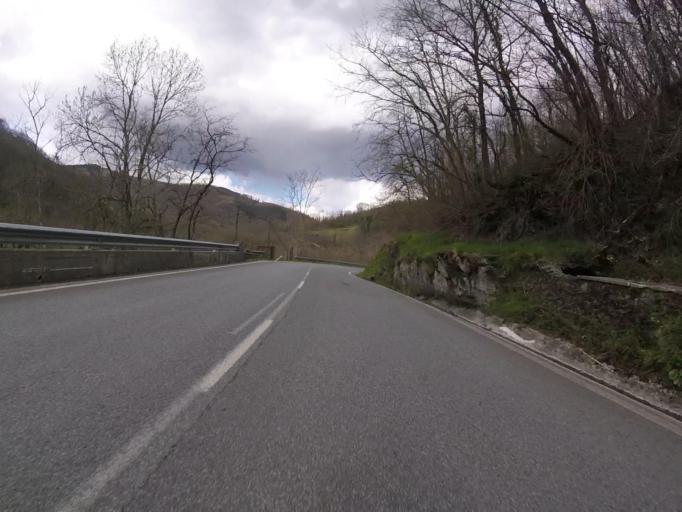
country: ES
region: Navarre
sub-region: Provincia de Navarra
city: Etxalar
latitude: 43.2379
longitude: -1.6611
